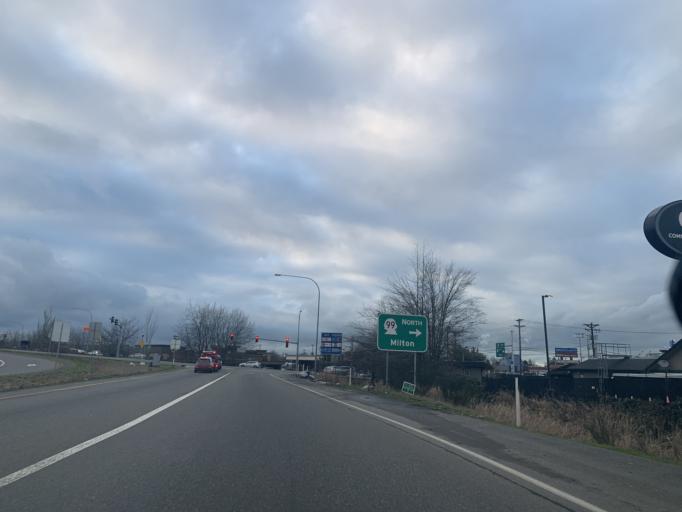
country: US
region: Washington
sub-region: Pierce County
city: Fife
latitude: 47.2422
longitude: -122.3558
